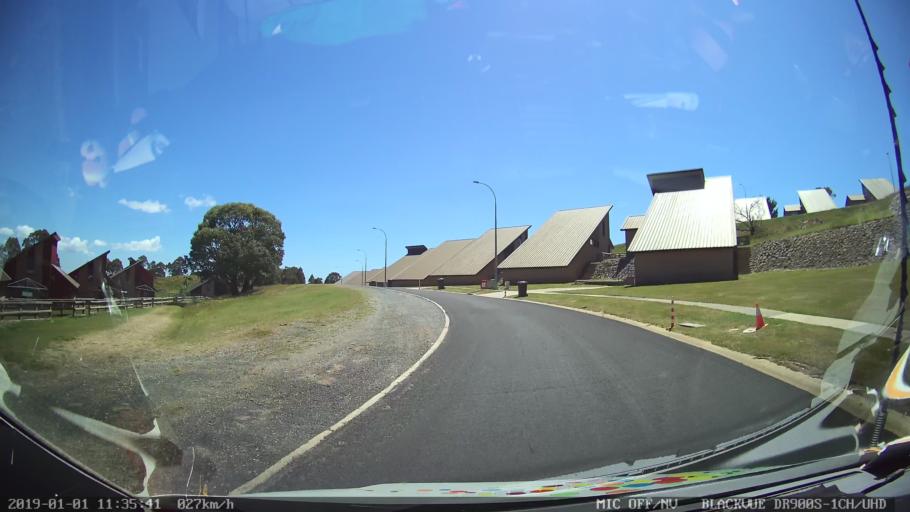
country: AU
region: New South Wales
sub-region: Snowy River
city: Jindabyne
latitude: -35.9342
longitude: 148.3804
